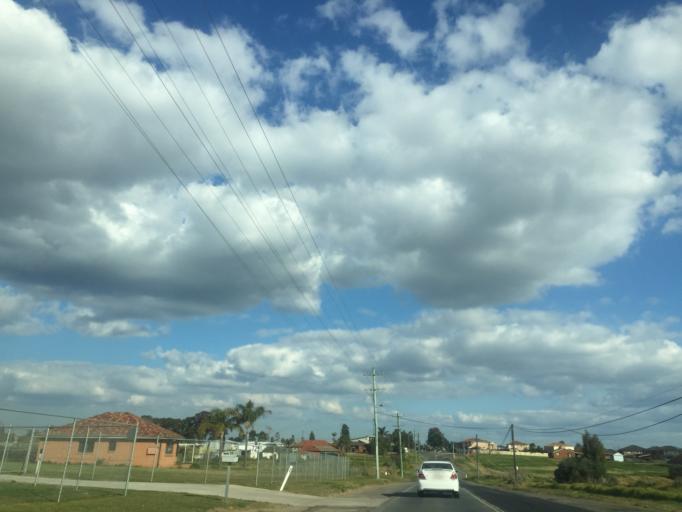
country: AU
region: New South Wales
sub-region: Blacktown
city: Quakers Hill
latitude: -33.7098
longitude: 150.8935
